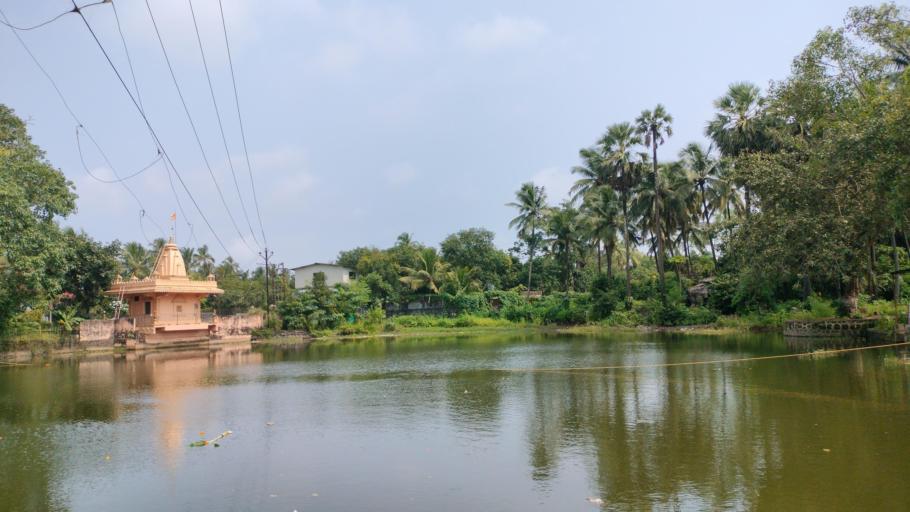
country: IN
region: Maharashtra
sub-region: Thane
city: Bhayandar
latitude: 19.3627
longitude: 72.7978
